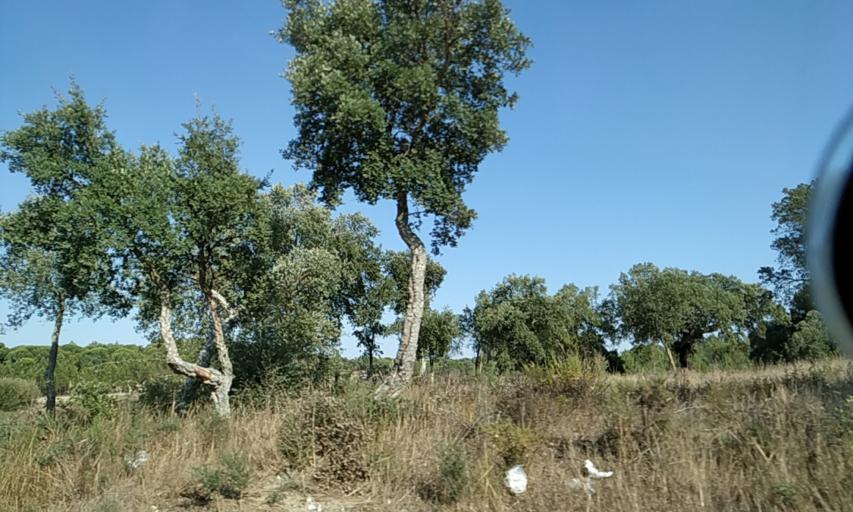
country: PT
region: Santarem
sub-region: Coruche
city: Coruche
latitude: 38.8845
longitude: -8.5375
